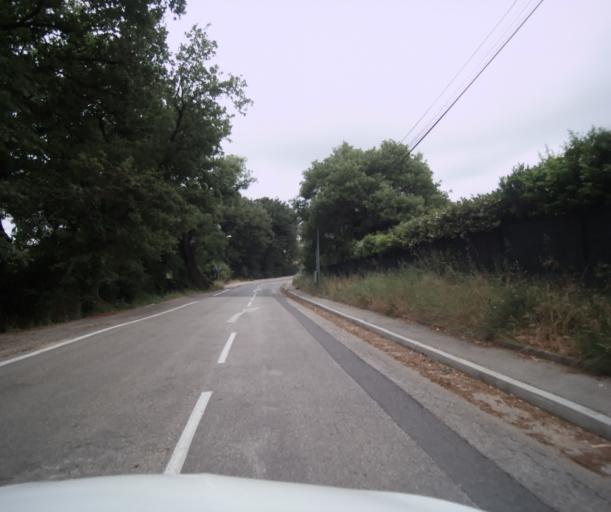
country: FR
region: Provence-Alpes-Cote d'Azur
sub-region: Departement du Var
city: Ollioules
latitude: 43.1369
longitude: 5.8720
